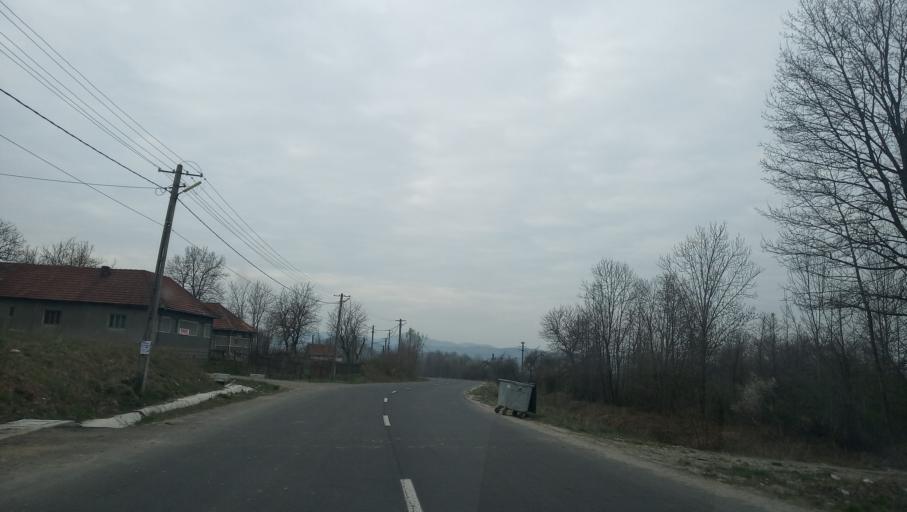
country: RO
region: Arad
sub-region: Comuna Varfurile
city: Varfurile
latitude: 46.3285
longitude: 22.5521
